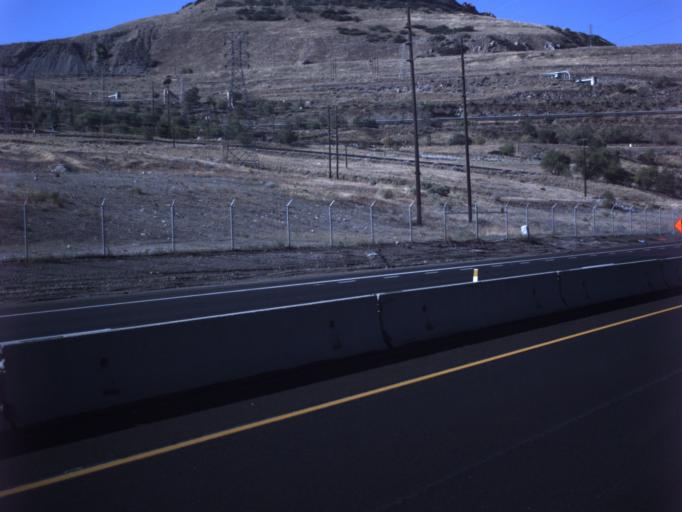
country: US
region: Utah
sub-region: Salt Lake County
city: Magna
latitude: 40.7165
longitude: -112.1235
